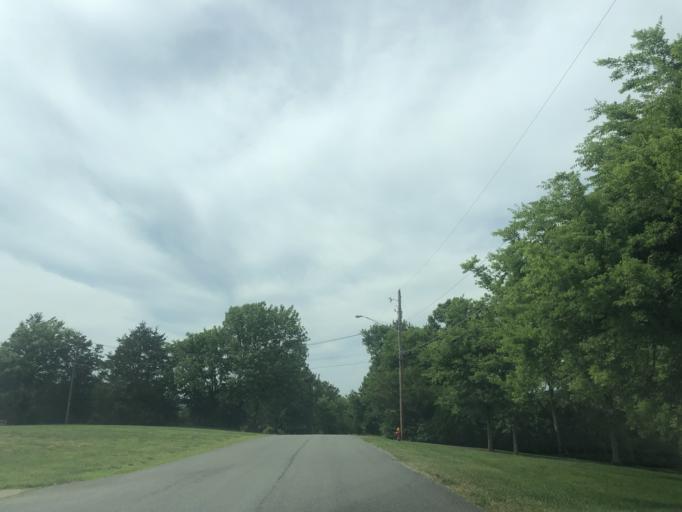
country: US
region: Tennessee
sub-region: Davidson County
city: Nashville
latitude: 36.2145
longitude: -86.8087
